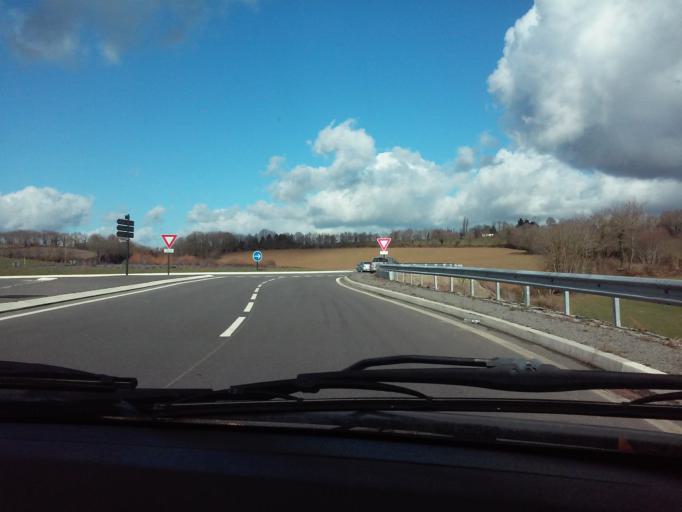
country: FR
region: Brittany
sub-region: Departement d'Ille-et-Vilaine
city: Vitre
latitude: 48.0951
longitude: -1.2257
